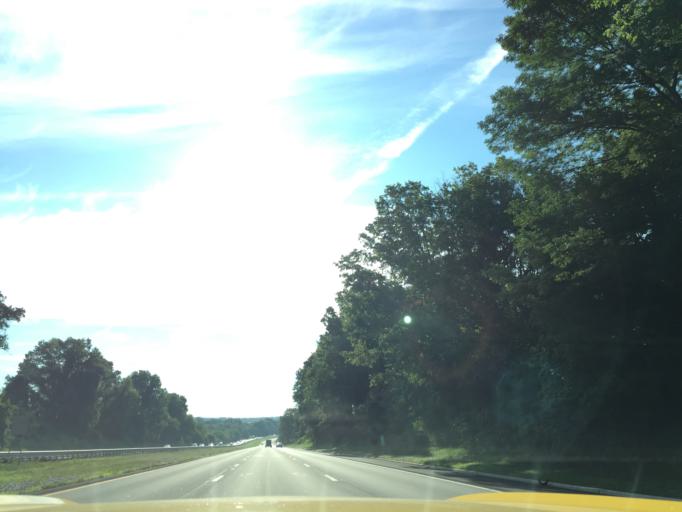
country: US
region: New Jersey
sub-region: Hunterdon County
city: Lebanon
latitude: 40.6464
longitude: -74.8502
